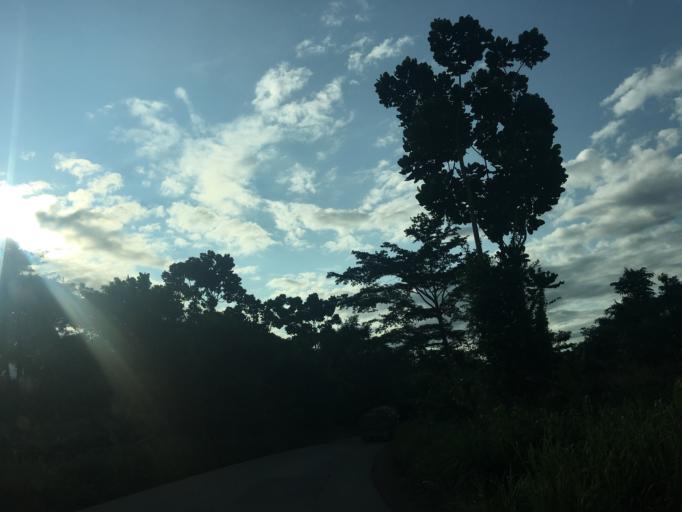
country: GH
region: Western
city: Bibiani
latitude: 6.2844
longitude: -2.2290
